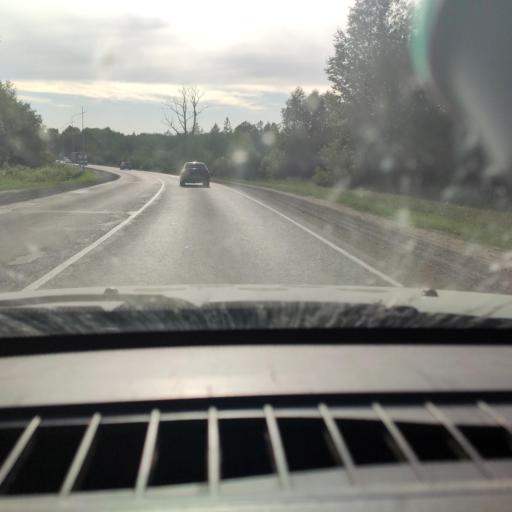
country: RU
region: Kirov
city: Vakhrushi
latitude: 58.6514
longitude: 49.8830
